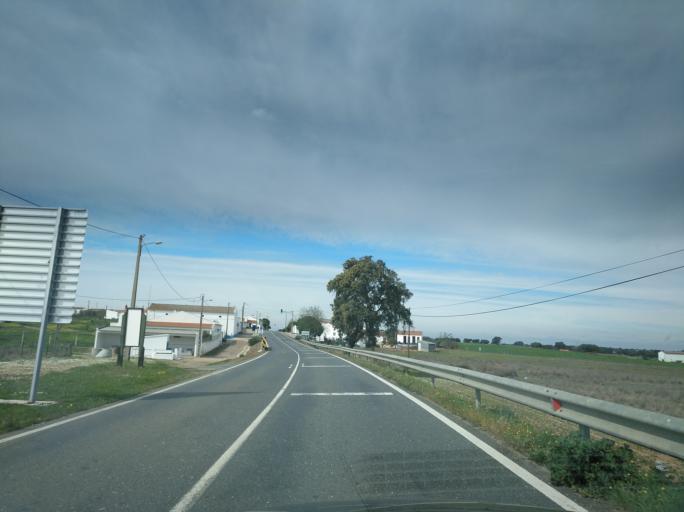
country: PT
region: Beja
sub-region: Mertola
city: Mertola
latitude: 37.7599
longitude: -7.8131
